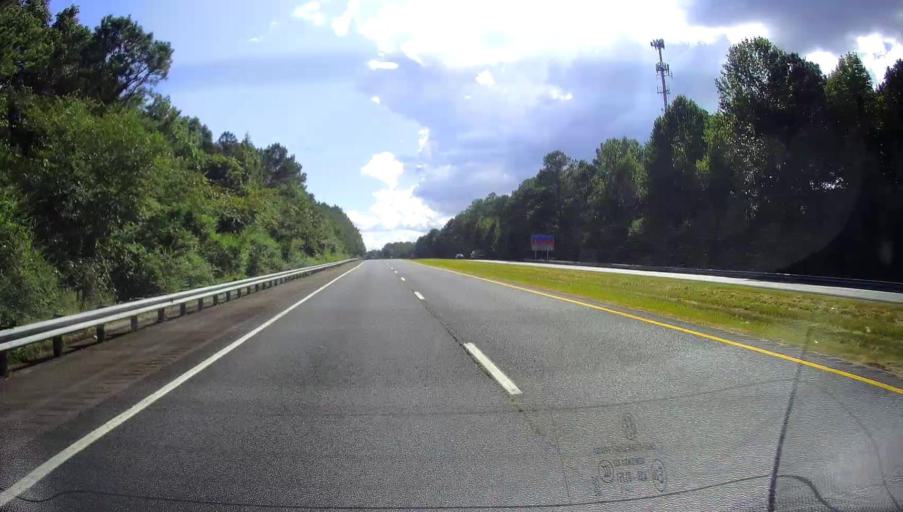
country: US
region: Georgia
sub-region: Muscogee County
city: Columbus
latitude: 32.5477
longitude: -84.8638
